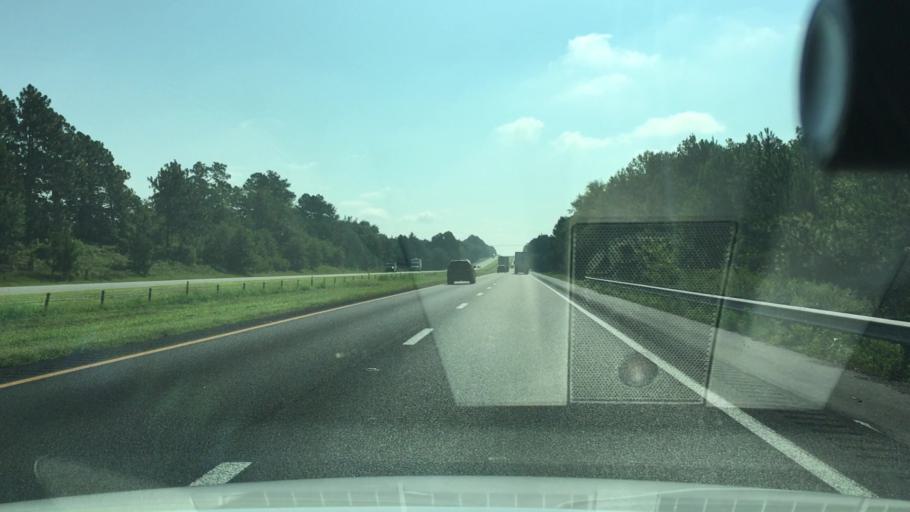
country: US
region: South Carolina
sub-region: Aiken County
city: Graniteville
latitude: 33.6338
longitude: -81.7807
